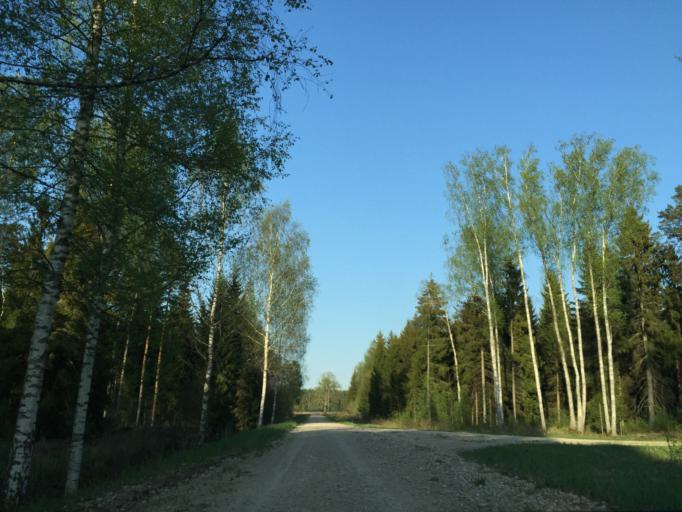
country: LV
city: Tireli
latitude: 56.8379
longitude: 23.7135
